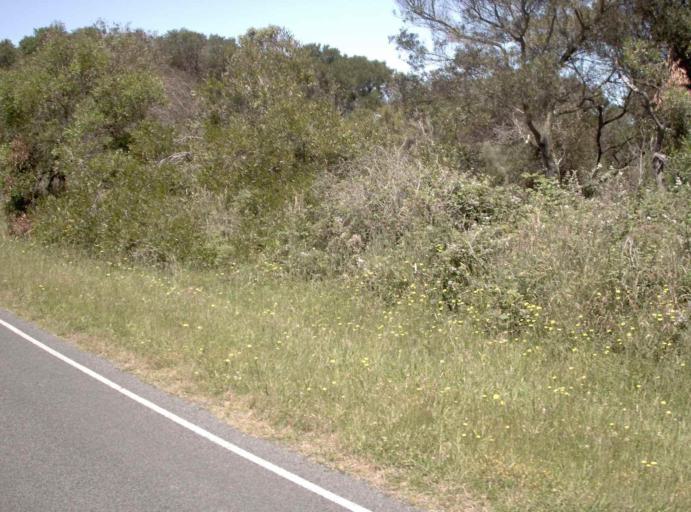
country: AU
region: Victoria
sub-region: Latrobe
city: Morwell
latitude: -38.7956
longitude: 146.1837
